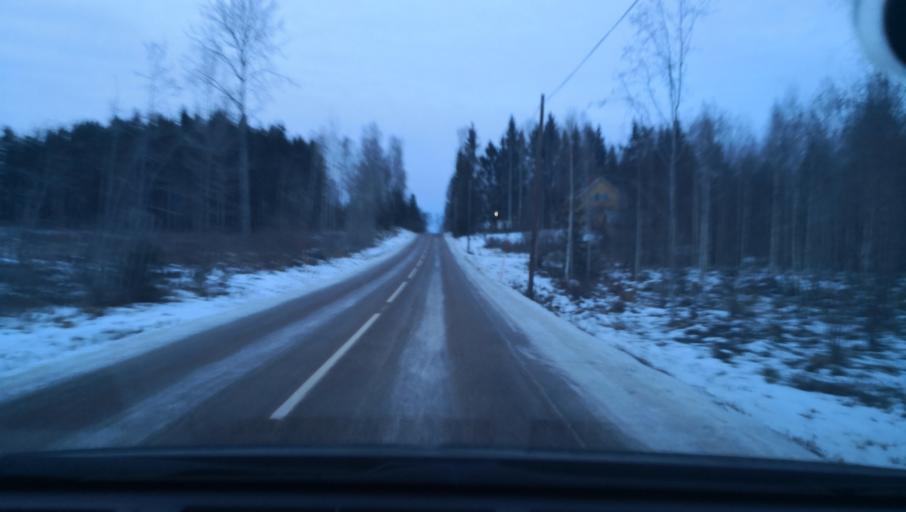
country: SE
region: Dalarna
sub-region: Avesta Kommun
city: Horndal
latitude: 60.1931
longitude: 16.4665
